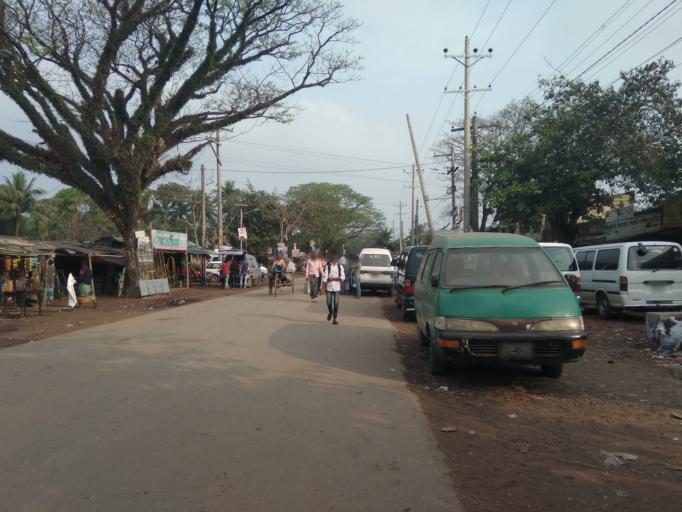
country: IN
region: West Bengal
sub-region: North 24 Parganas
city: Taki
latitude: 22.3446
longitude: 89.1046
